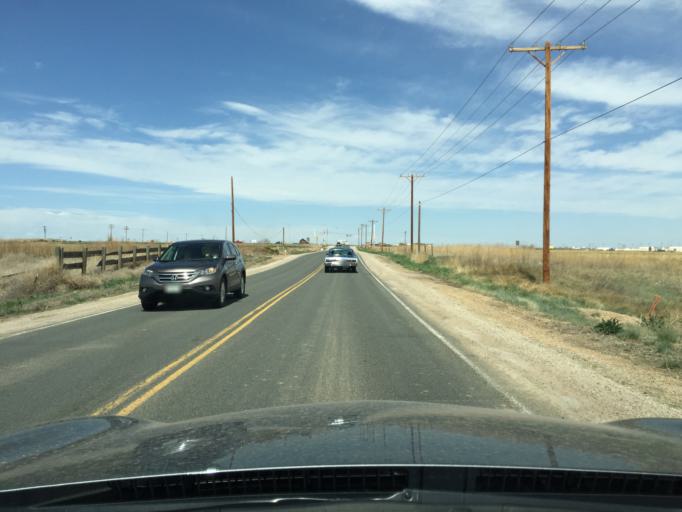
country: US
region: Colorado
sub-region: Boulder County
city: Erie
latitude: 39.9971
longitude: -104.9972
